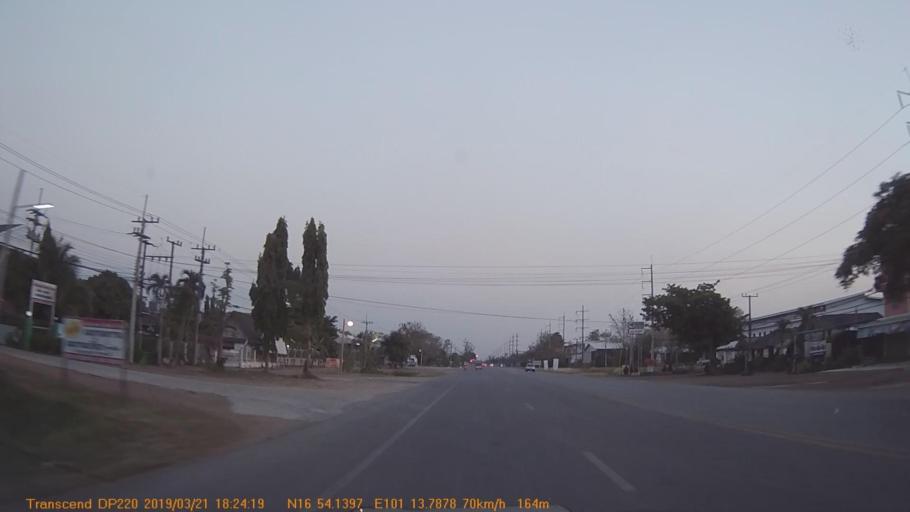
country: TH
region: Phetchabun
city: Lom Kao
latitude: 16.9021
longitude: 101.2298
